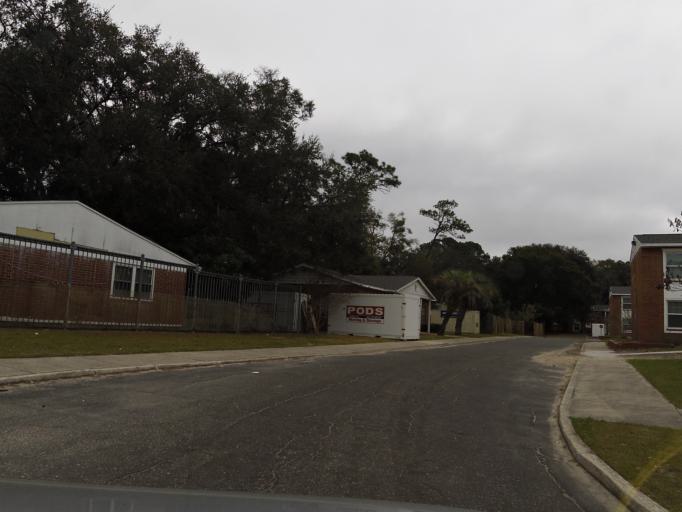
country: US
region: Florida
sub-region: Duval County
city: Jacksonville
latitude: 30.3908
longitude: -81.7160
